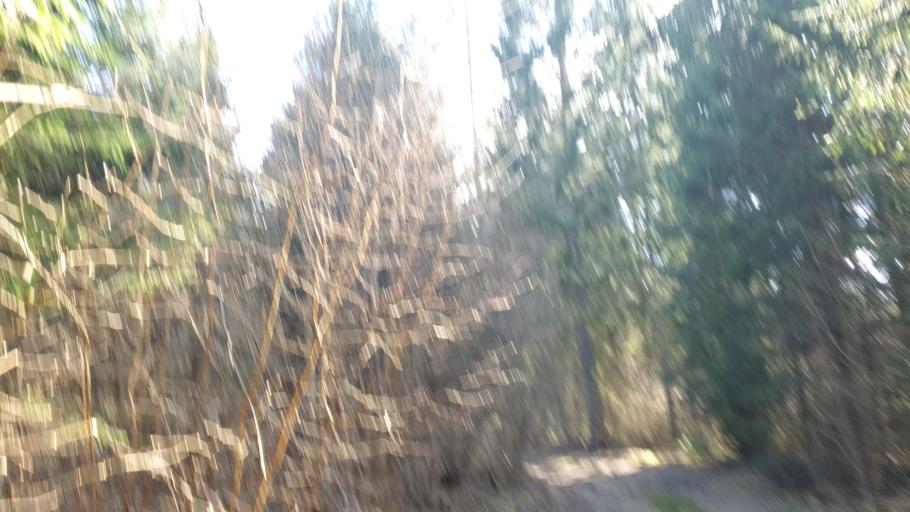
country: LT
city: Aukstadvaris
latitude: 54.4935
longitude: 24.6510
